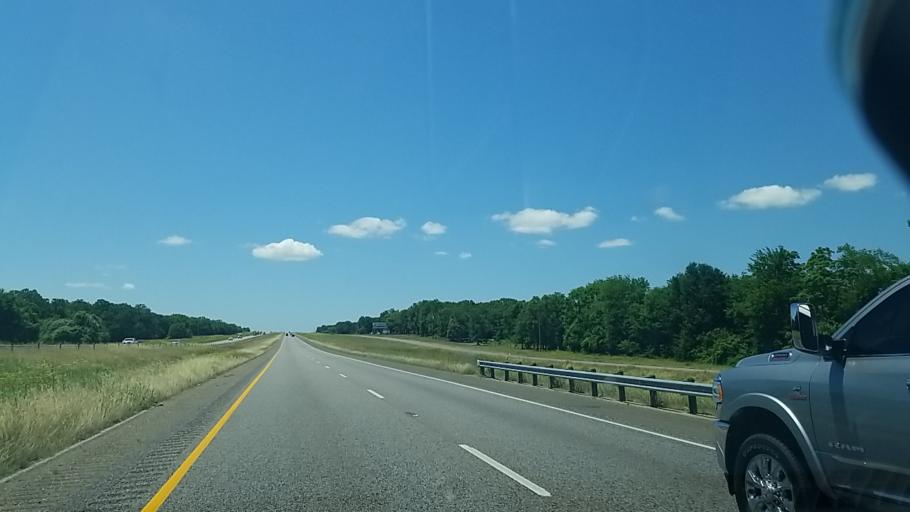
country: US
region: Texas
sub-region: Madison County
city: Madisonville
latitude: 30.9392
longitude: -95.8416
